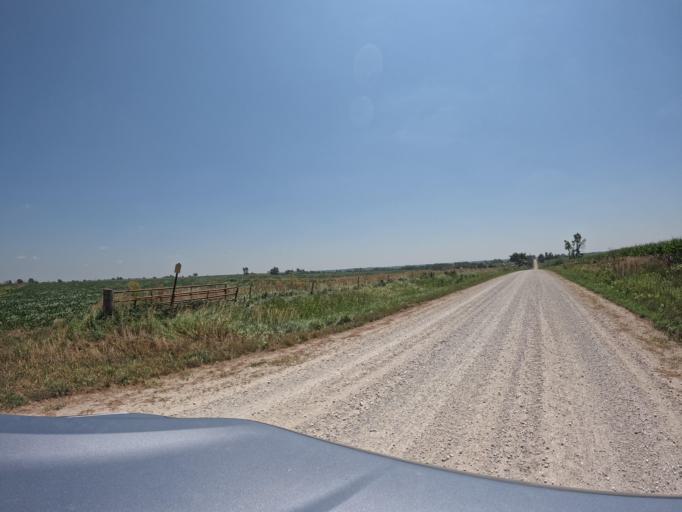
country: US
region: Iowa
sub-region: Keokuk County
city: Sigourney
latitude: 41.2685
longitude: -92.1807
